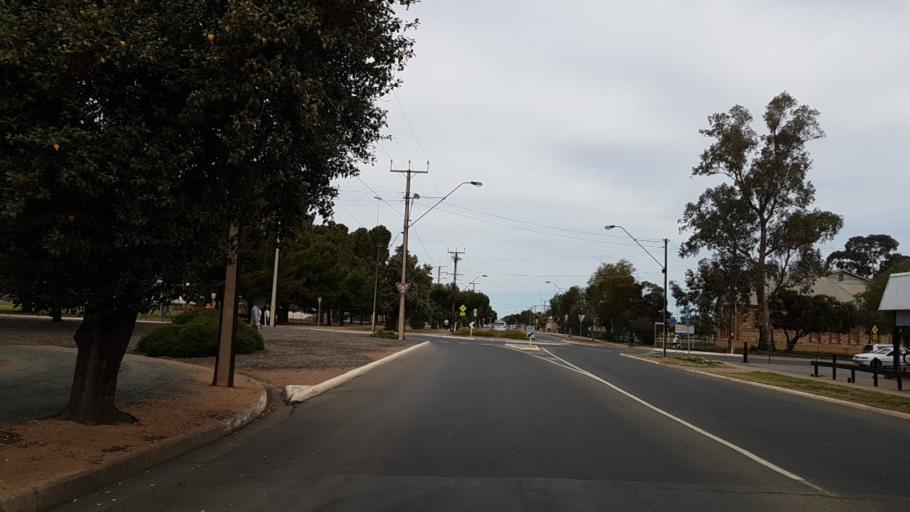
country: AU
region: South Australia
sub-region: Port Pirie City and Dists
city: Port Pirie
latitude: -33.1808
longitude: 138.0039
